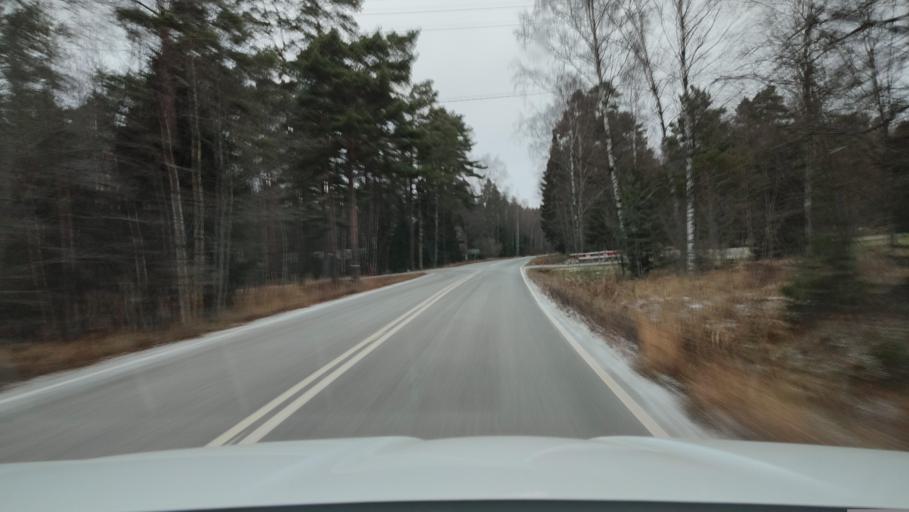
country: FI
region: Ostrobothnia
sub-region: Sydosterbotten
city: Kristinestad
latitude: 62.3195
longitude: 21.3497
